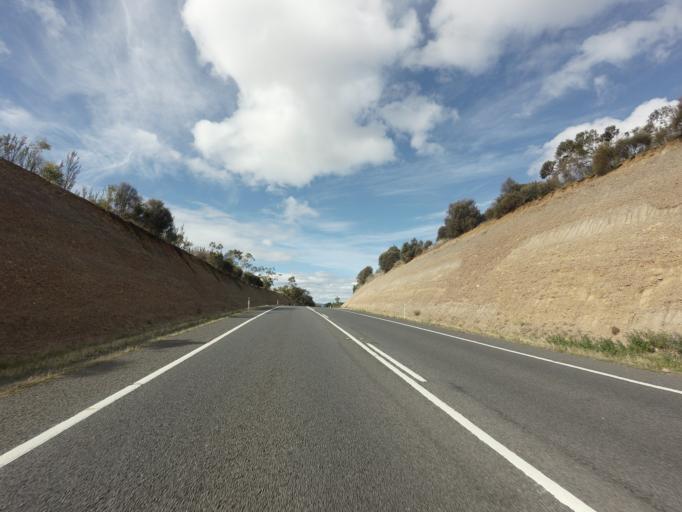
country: AU
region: Tasmania
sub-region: Brighton
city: Bridgewater
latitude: -42.7442
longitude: 147.1865
